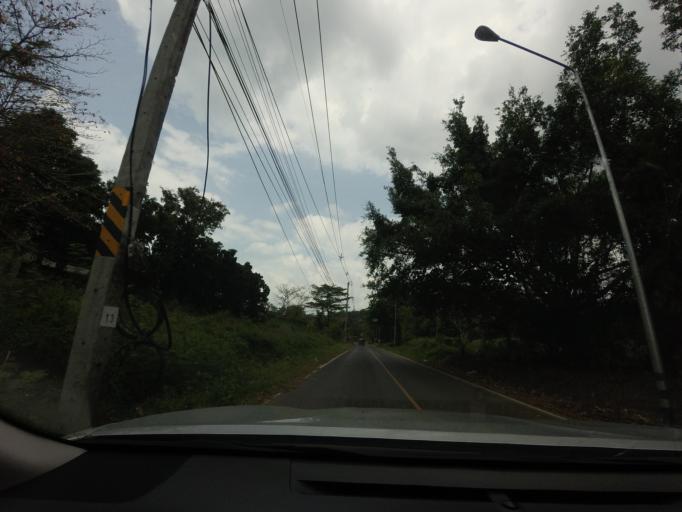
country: TH
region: Phangnga
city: Ban Ao Nang
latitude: 8.0739
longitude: 98.7459
